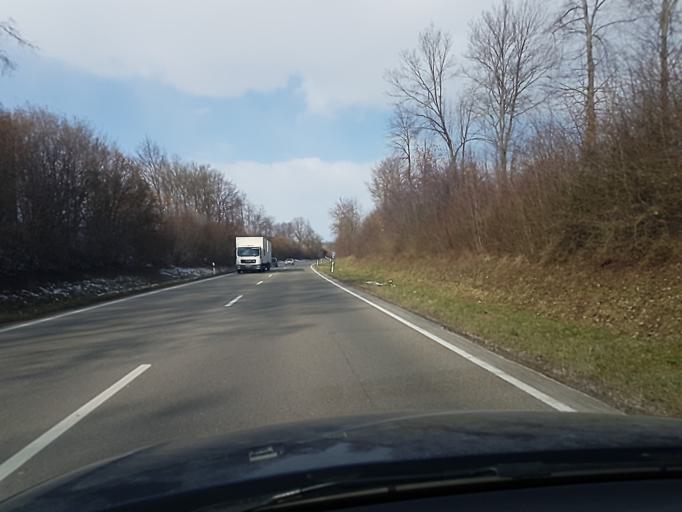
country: DE
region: Baden-Wuerttemberg
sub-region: Regierungsbezirk Stuttgart
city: Bondorf
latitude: 48.5241
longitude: 8.8441
